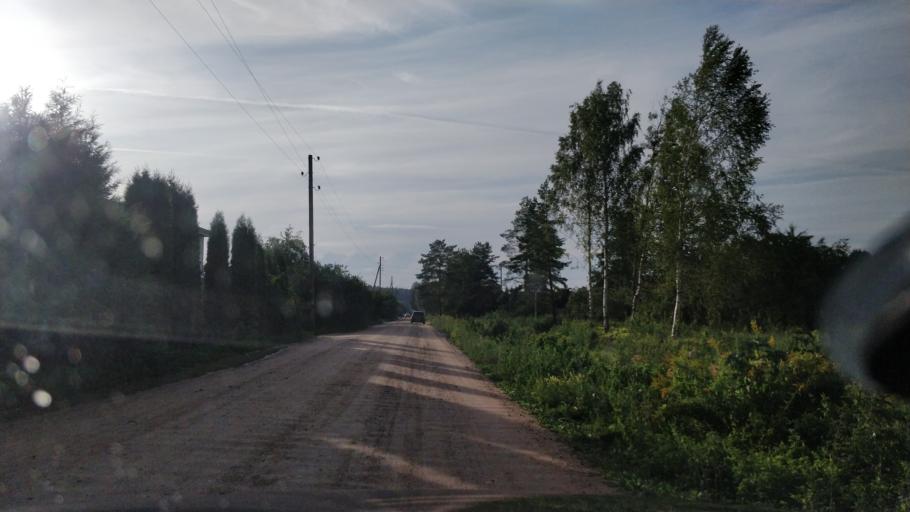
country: LV
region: Incukalns
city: Incukalns
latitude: 57.0984
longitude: 24.7541
